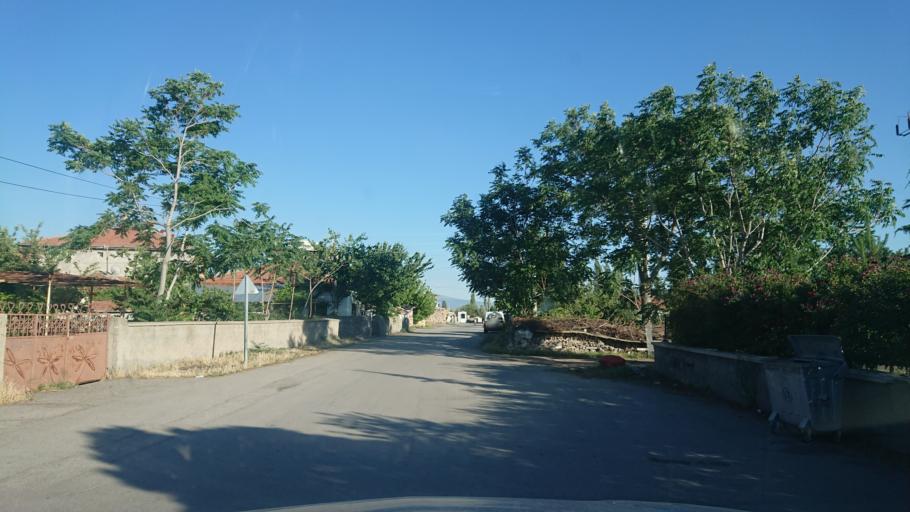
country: TR
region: Aksaray
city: Aksaray
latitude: 38.3846
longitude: 33.9906
